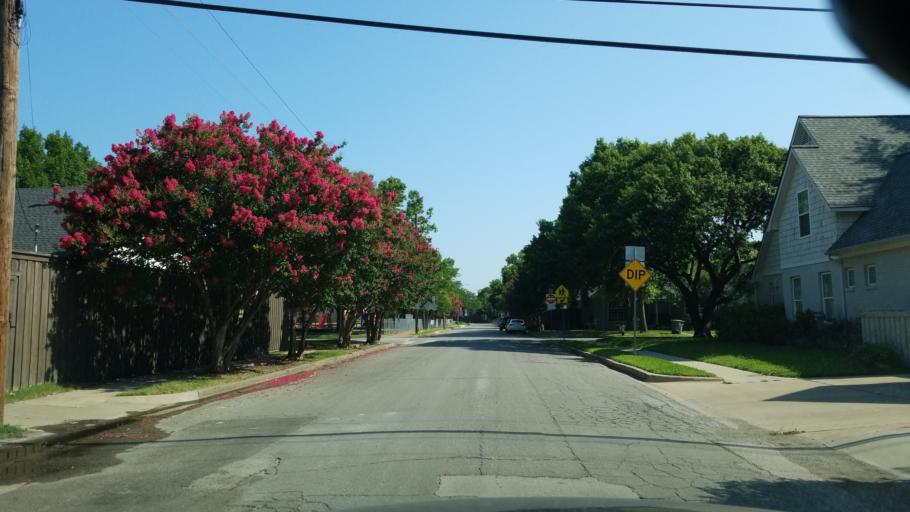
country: US
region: Texas
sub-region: Dallas County
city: Highland Park
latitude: 32.8343
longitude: -96.7657
